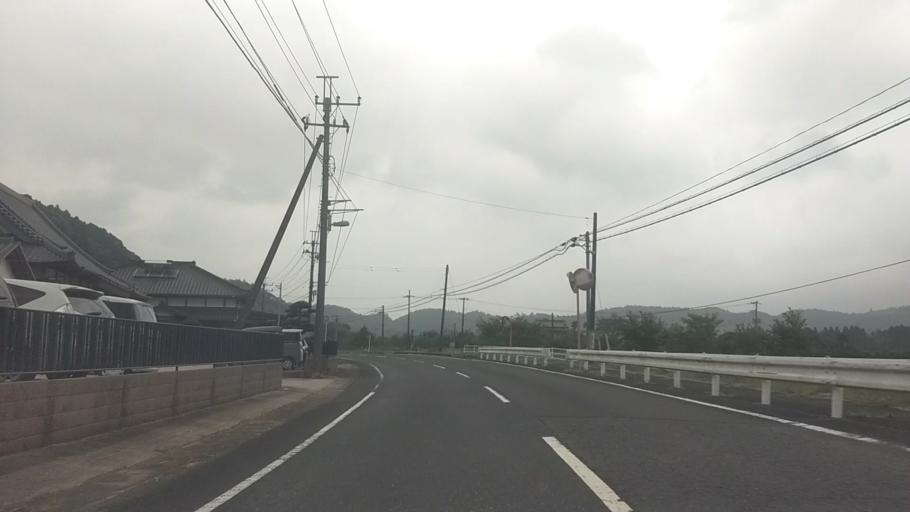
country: JP
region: Chiba
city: Katsuura
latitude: 35.2603
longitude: 140.2492
